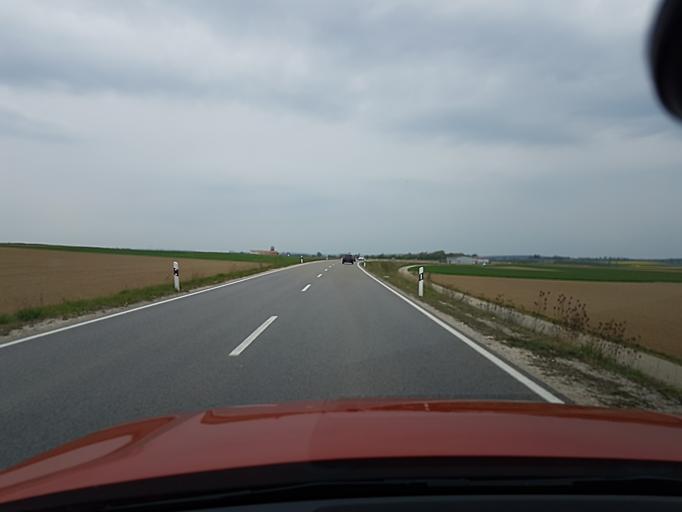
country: DE
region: Bavaria
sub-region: Upper Bavaria
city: Wettstetten
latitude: 48.8177
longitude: 11.3932
